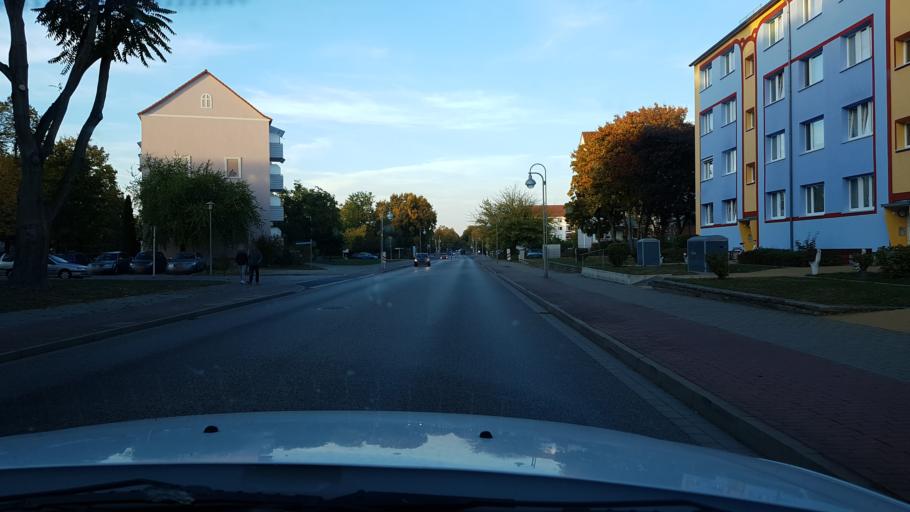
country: DE
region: Brandenburg
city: Schwedt (Oder)
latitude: 53.0597
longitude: 14.2946
